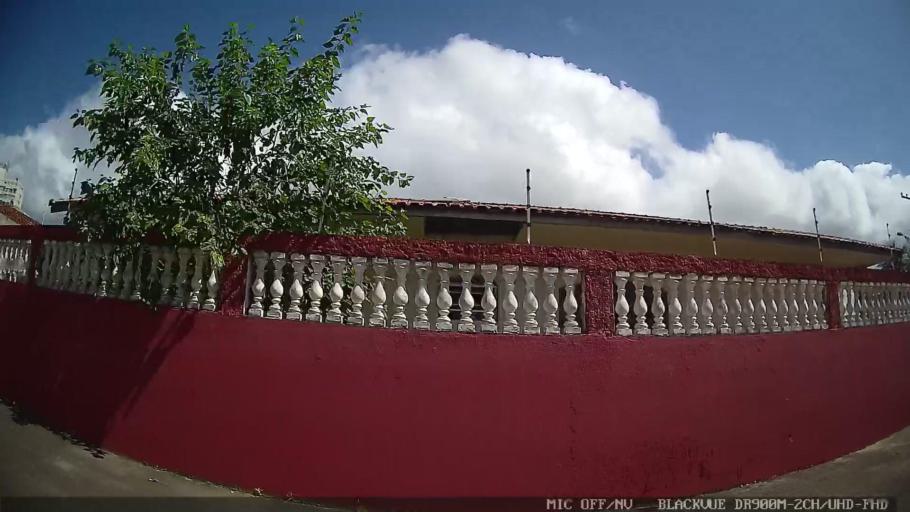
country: BR
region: Sao Paulo
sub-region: Peruibe
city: Peruibe
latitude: -24.3234
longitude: -46.9954
